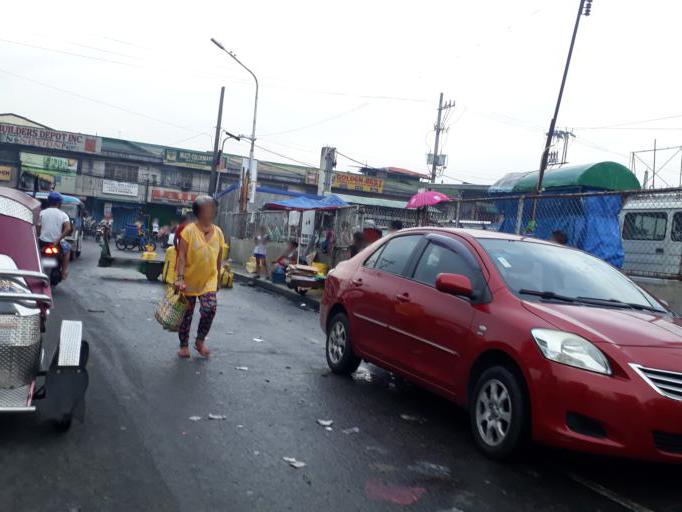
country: PH
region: Metro Manila
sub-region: Caloocan City
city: Niugan
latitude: 14.6567
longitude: 120.9514
